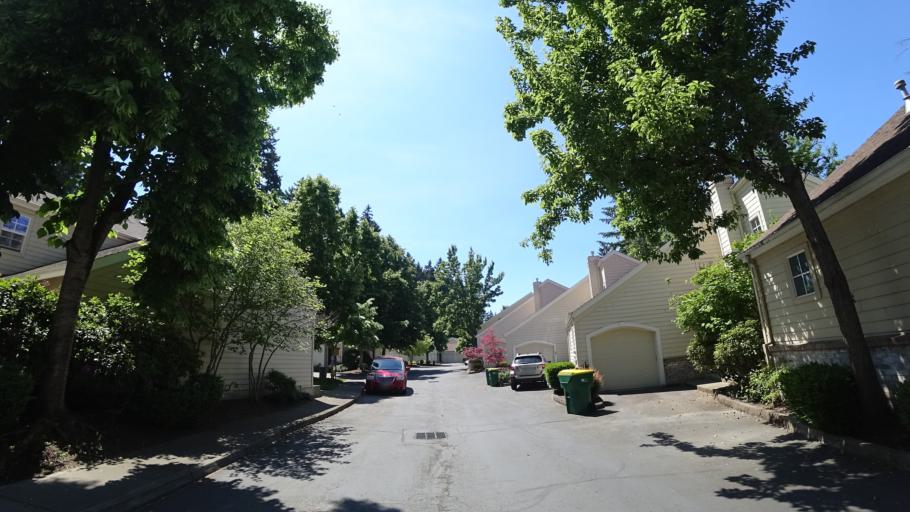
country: US
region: Oregon
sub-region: Washington County
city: King City
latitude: 45.4382
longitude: -122.8132
